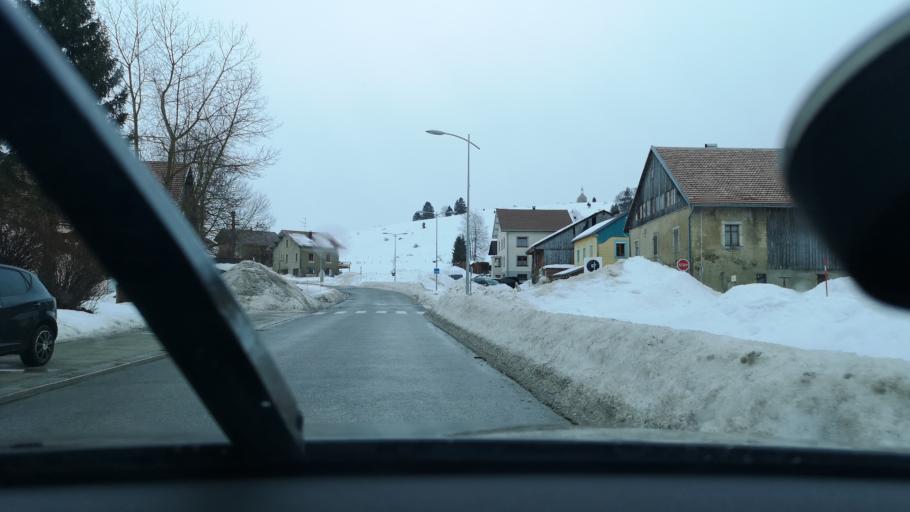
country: FR
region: Franche-Comte
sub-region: Departement du Doubs
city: Les Fourgs
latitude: 46.8334
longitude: 6.4078
